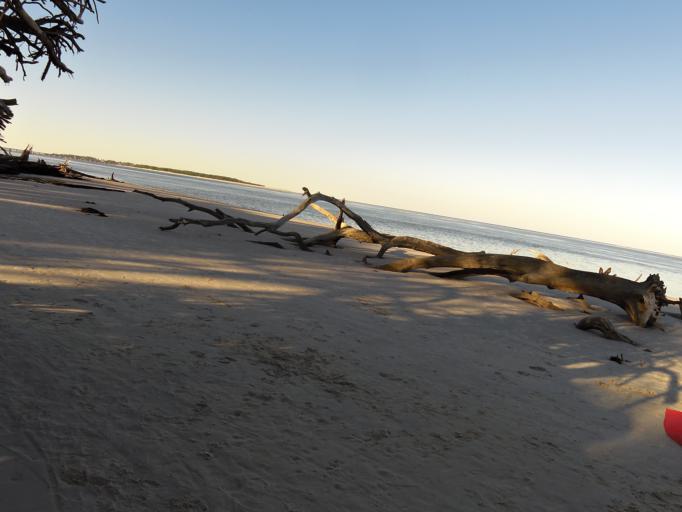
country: US
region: Florida
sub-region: Duval County
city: Atlantic Beach
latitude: 30.4912
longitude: -81.4386
